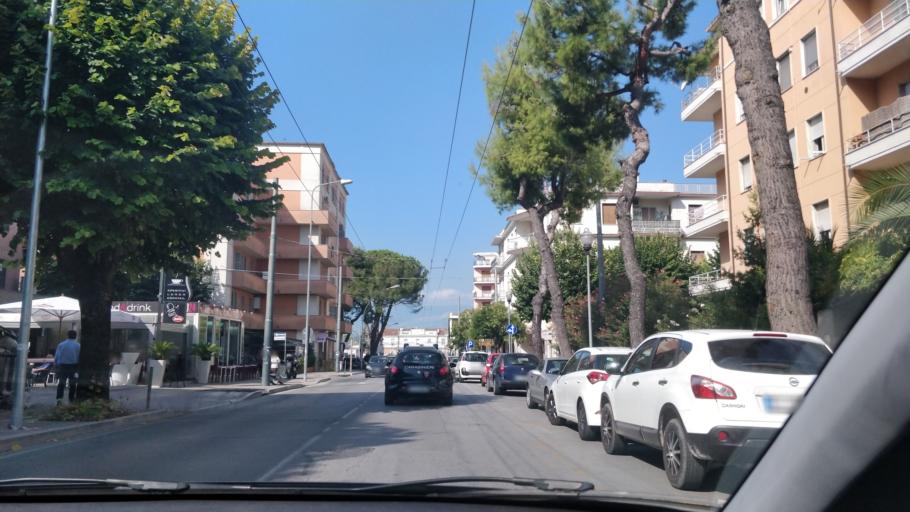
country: IT
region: Abruzzo
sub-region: Provincia di Chieti
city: Chieti
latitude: 42.3569
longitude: 14.1411
